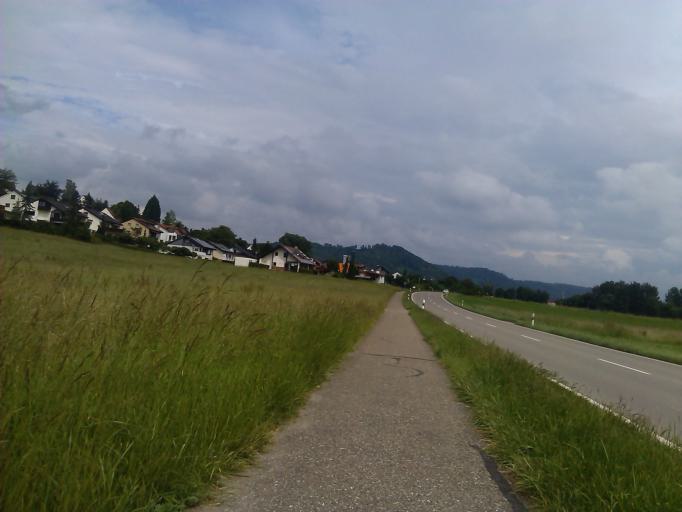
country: DE
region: Baden-Wuerttemberg
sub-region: Regierungsbezirk Stuttgart
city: Gaildorf
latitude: 48.9824
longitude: 9.7653
